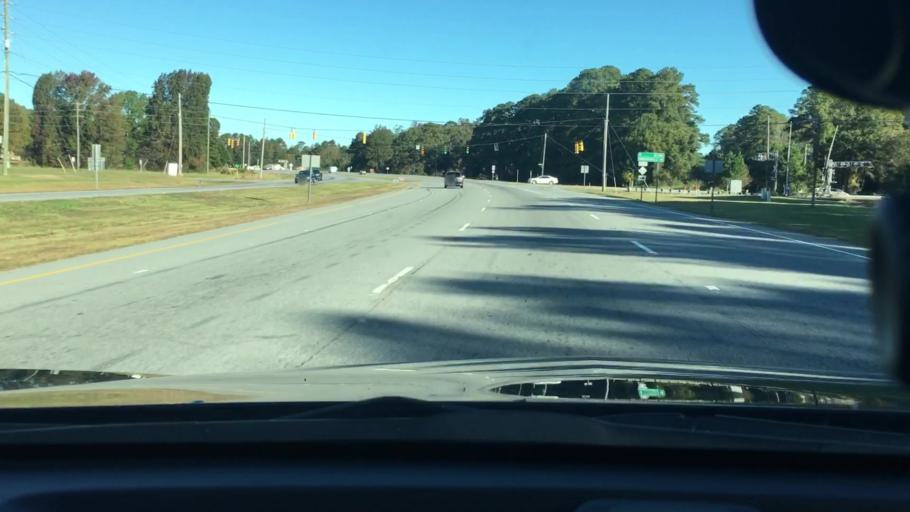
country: US
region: North Carolina
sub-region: Pitt County
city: Greenville
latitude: 35.6679
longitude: -77.3609
